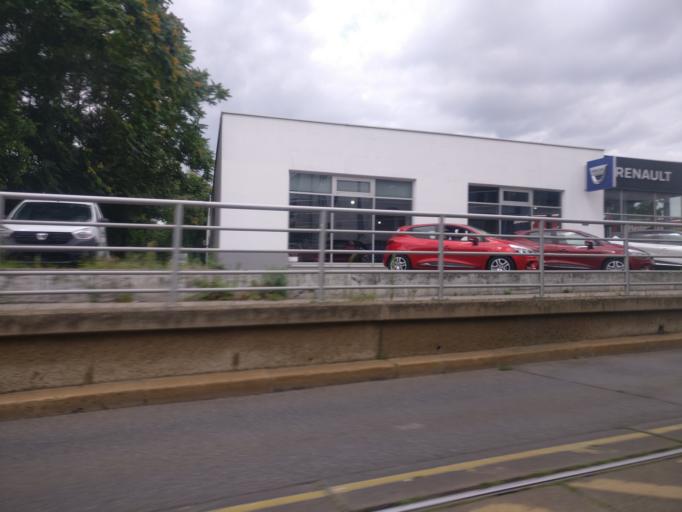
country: AT
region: Vienna
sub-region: Wien Stadt
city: Vienna
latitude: 48.2382
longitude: 16.3746
